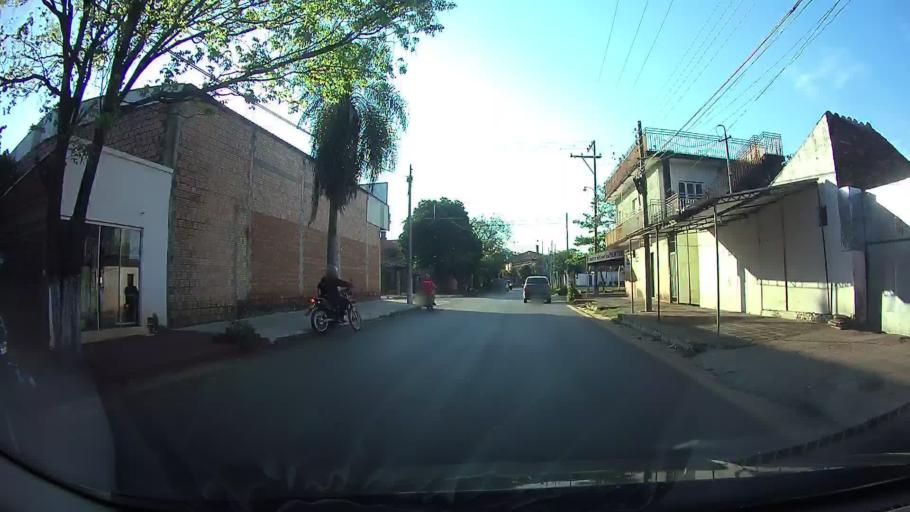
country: PY
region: Central
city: Fernando de la Mora
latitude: -25.3422
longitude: -57.5358
